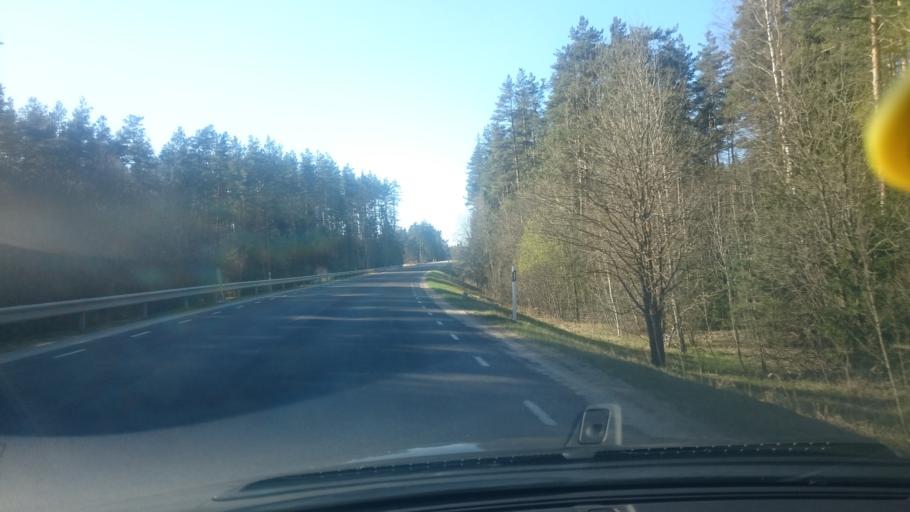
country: EE
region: Harju
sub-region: Raasiku vald
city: Raasiku
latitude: 59.1589
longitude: 25.1847
